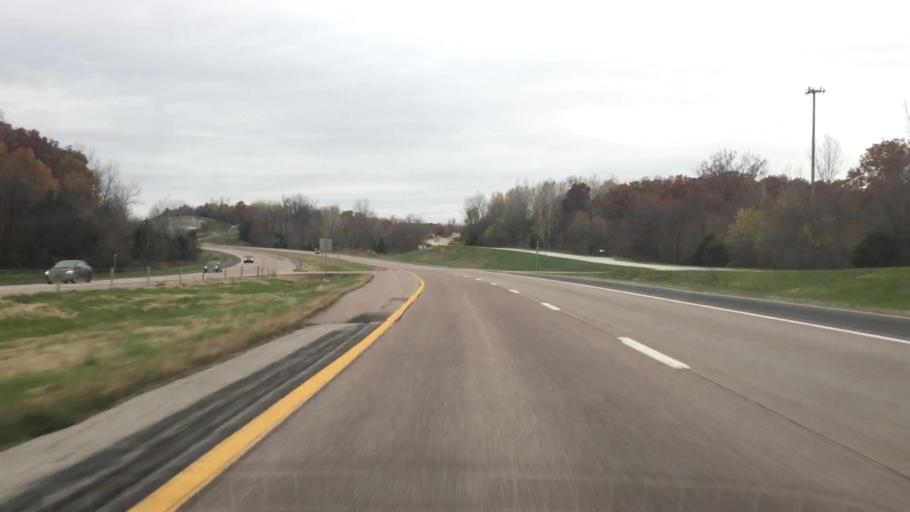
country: US
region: Missouri
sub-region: Cole County
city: Jefferson City
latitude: 38.6668
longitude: -92.2282
